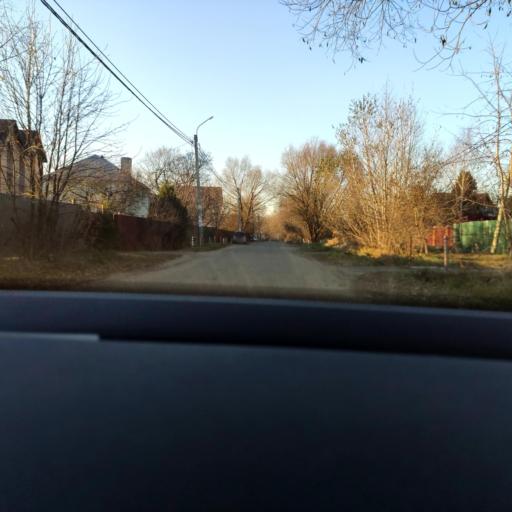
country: RU
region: Moscow
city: Gol'yanovo
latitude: 55.8297
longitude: 37.8404
